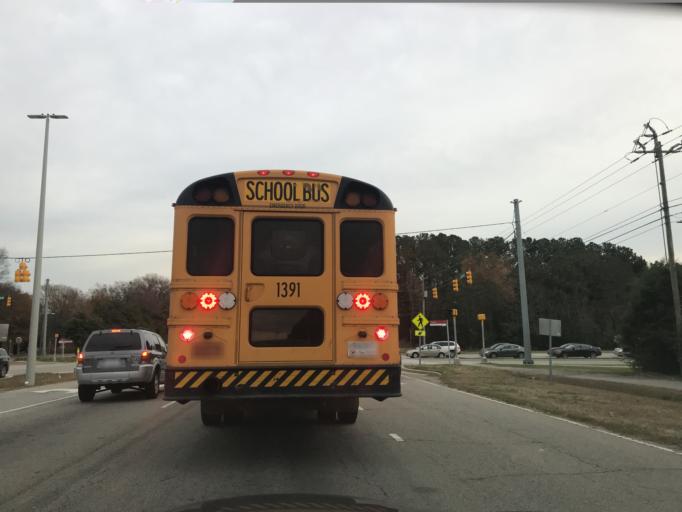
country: US
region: North Carolina
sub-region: Wake County
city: West Raleigh
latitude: 35.7839
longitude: -78.6830
